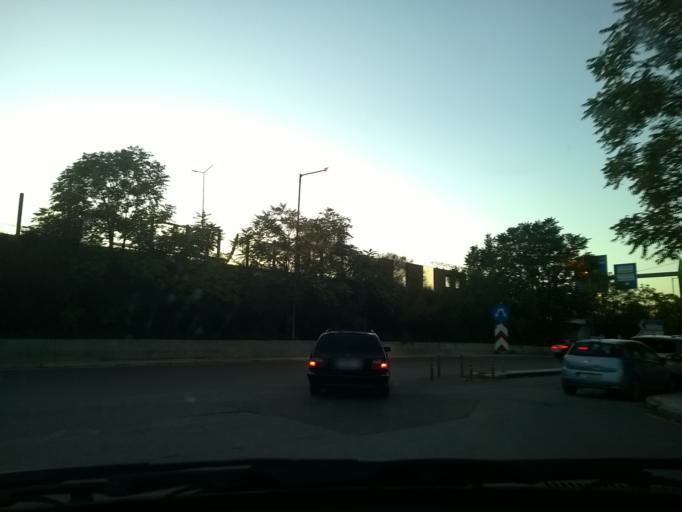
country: GR
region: Central Macedonia
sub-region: Nomos Thessalonikis
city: Polichni
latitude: 40.6739
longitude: 22.9610
